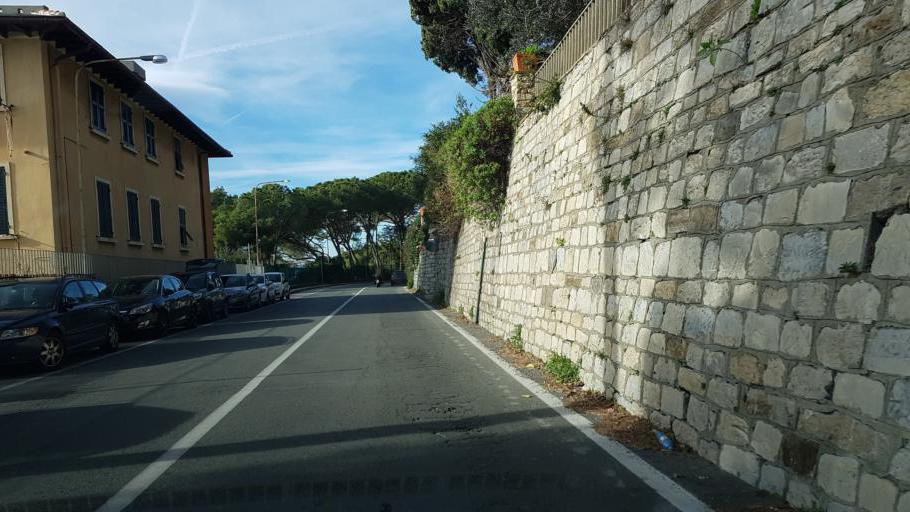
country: IT
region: Liguria
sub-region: Provincia di Genova
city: Sori
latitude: 44.3661
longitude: 9.1197
